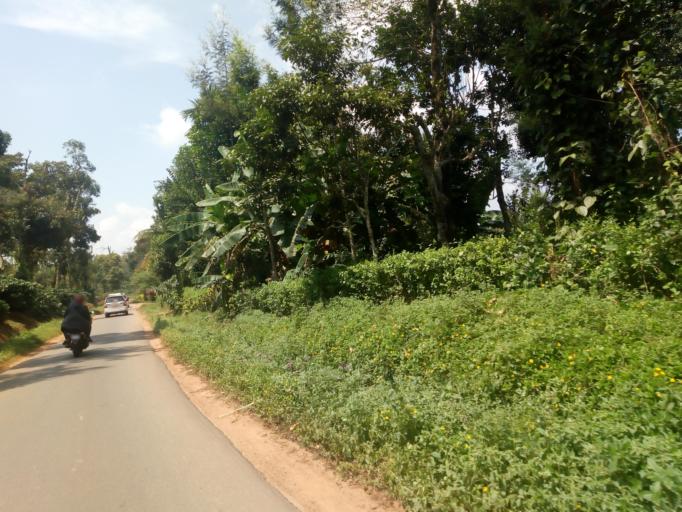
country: IN
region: Karnataka
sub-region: Kodagu
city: Ponnampet
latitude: 12.0308
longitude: 75.9592
